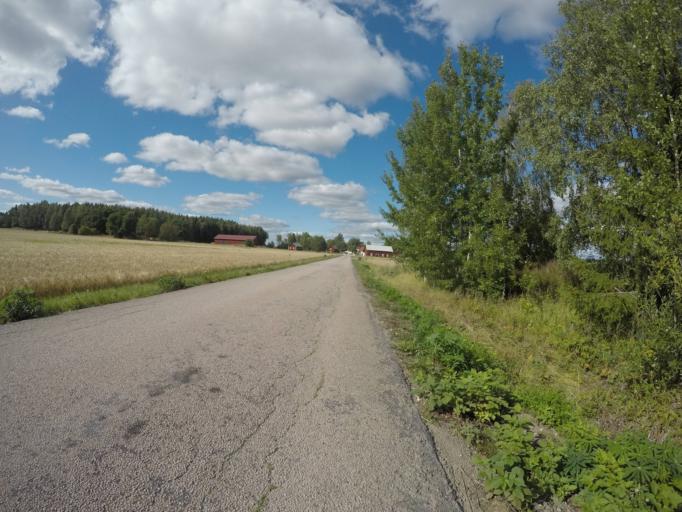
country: SE
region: Vaestmanland
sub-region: Hallstahammars Kommun
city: Kolback
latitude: 59.5125
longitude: 16.1875
